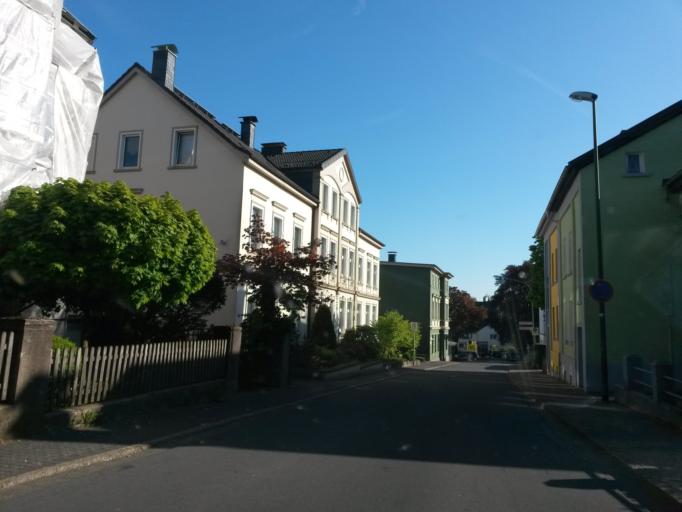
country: DE
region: North Rhine-Westphalia
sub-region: Regierungsbezirk Arnsberg
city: Luedenscheid
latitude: 51.2137
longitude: 7.6377
